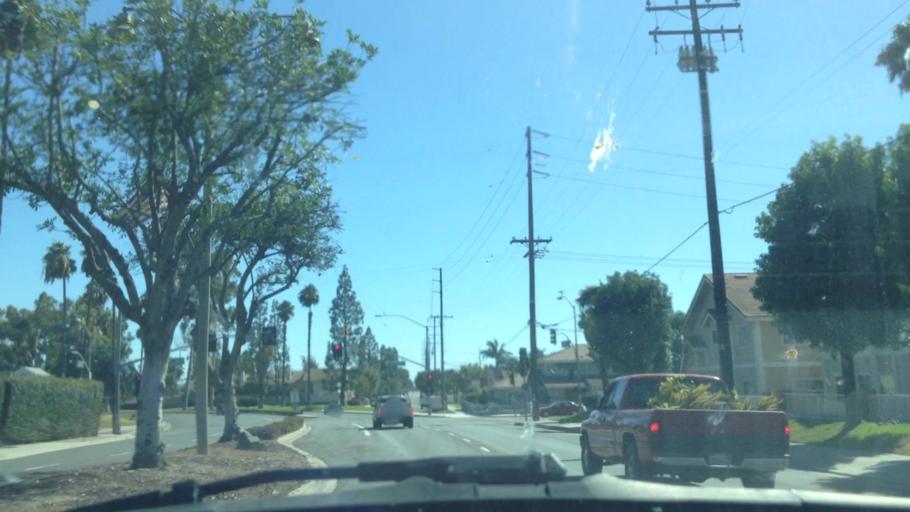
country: US
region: California
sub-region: Orange County
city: Placentia
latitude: 33.8809
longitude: -117.8635
